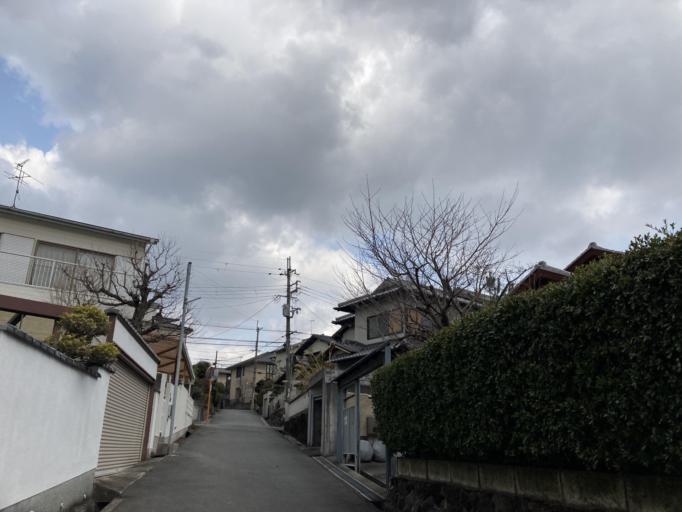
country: JP
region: Nara
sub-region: Ikoma-shi
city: Ikoma
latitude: 34.6098
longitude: 135.7253
